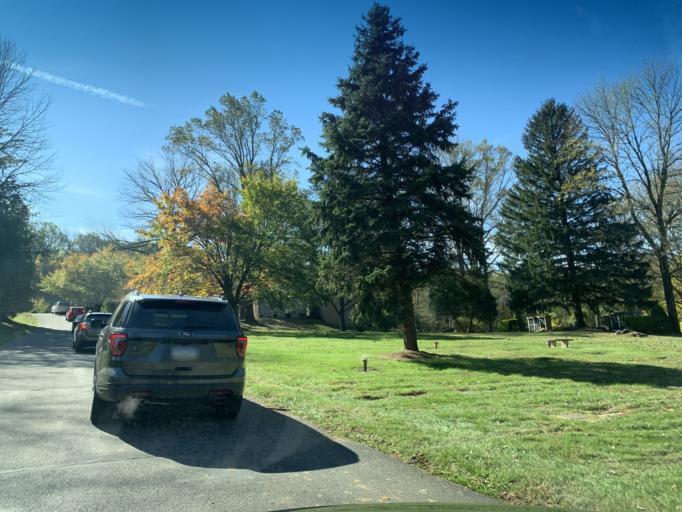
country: US
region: Pennsylvania
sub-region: Berks County
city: Mount Penn
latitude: 40.3130
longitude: -75.8922
